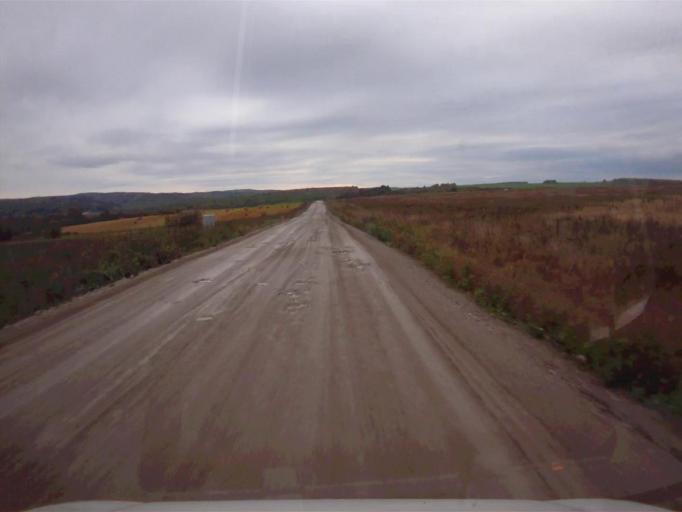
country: RU
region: Sverdlovsk
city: Mikhaylovsk
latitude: 56.1803
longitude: 59.1940
